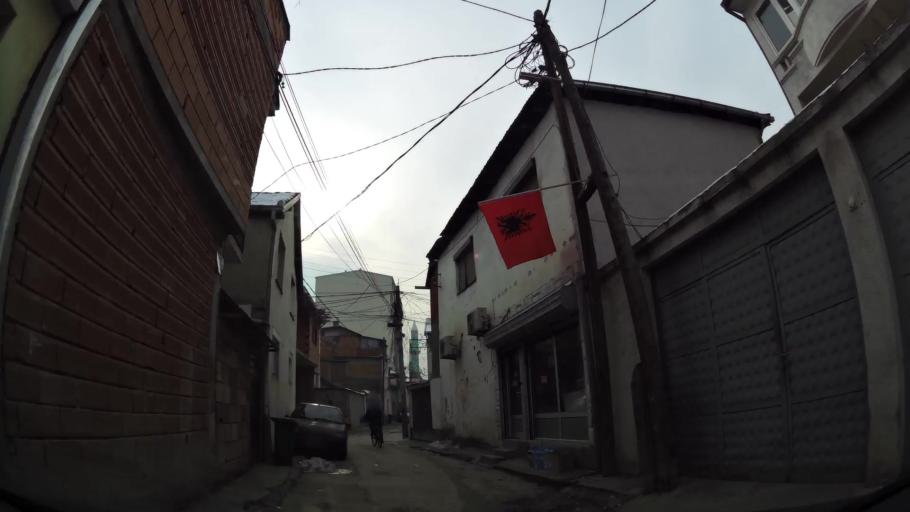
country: MK
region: Cair
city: Cair
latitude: 42.0065
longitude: 21.4444
